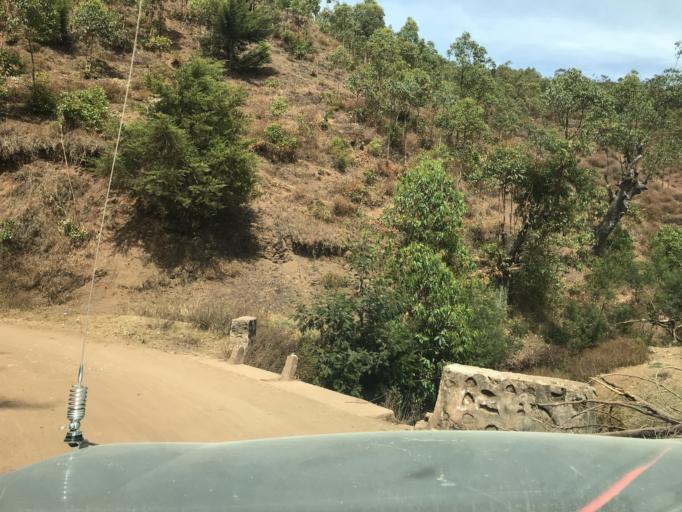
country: TL
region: Ainaro
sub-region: Ainaro
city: Ainaro
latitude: -8.8909
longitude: 125.5178
